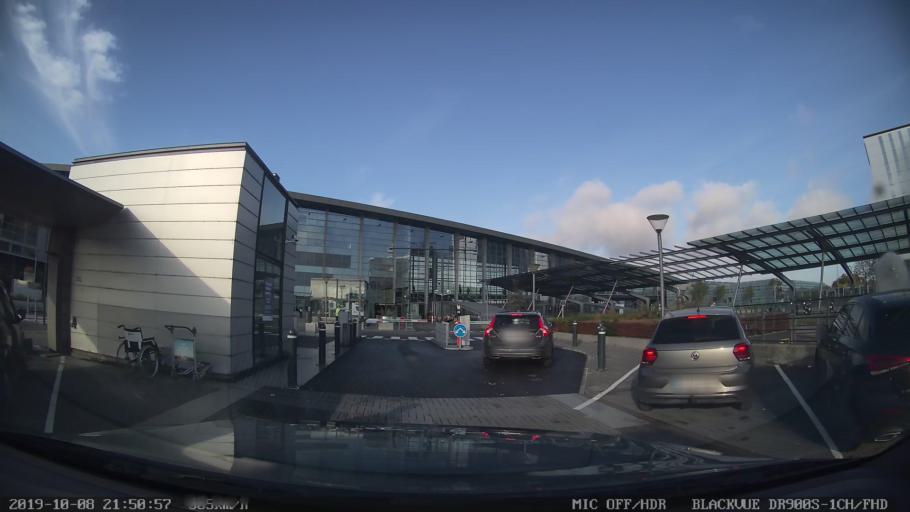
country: DK
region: Capital Region
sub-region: Dragor Kommune
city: Dragor
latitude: 55.6281
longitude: 12.6665
